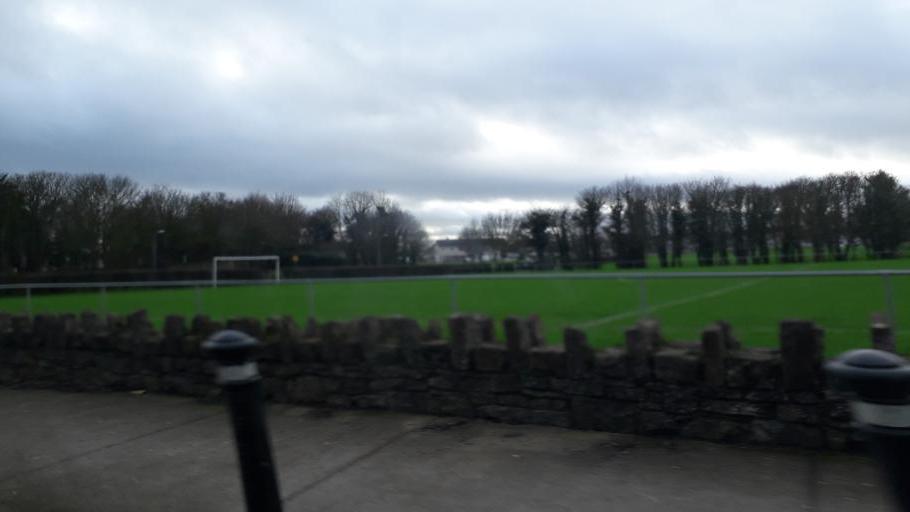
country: IE
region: Leinster
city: An Ros
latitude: 53.5392
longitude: -6.0928
